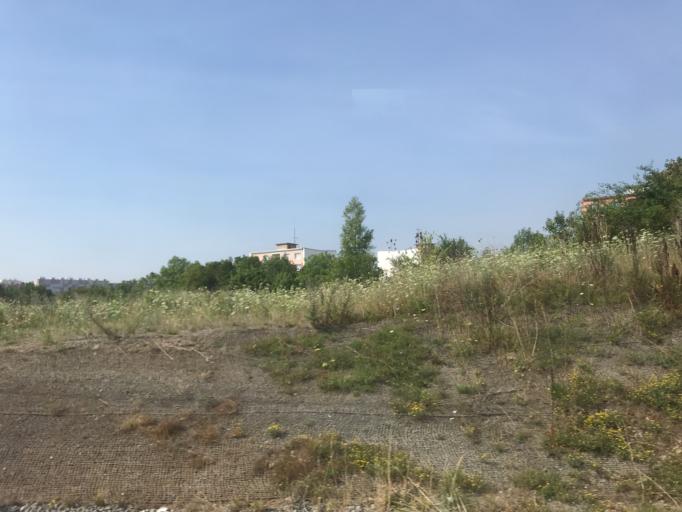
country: CZ
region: Praha
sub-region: Praha 14
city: Hostavice
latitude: 50.0571
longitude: 14.5237
